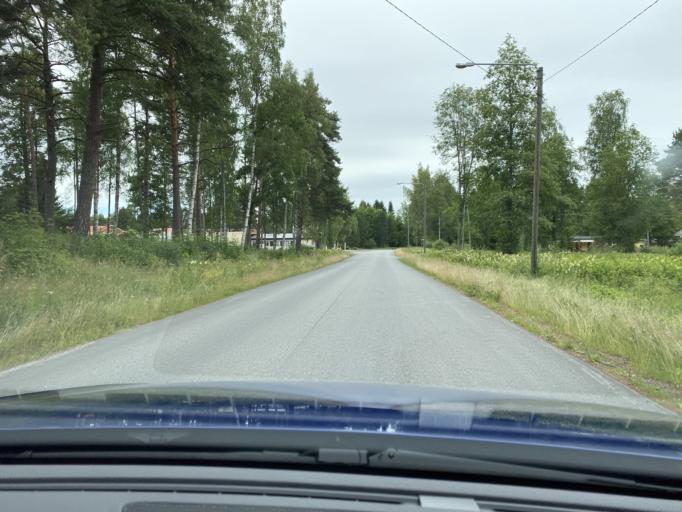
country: FI
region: Satakunta
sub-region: Rauma
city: Eura
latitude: 61.1089
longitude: 22.1442
